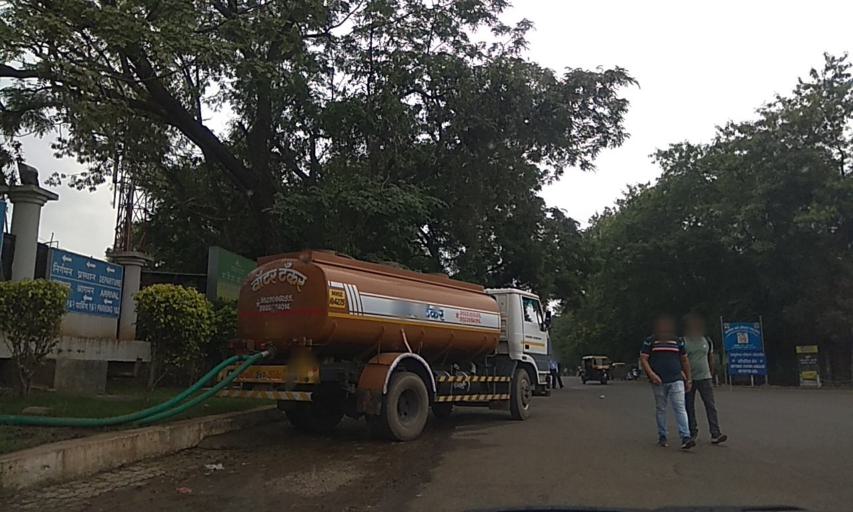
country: IN
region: Maharashtra
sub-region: Pune Division
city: Lohogaon
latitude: 18.5782
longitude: 73.9079
